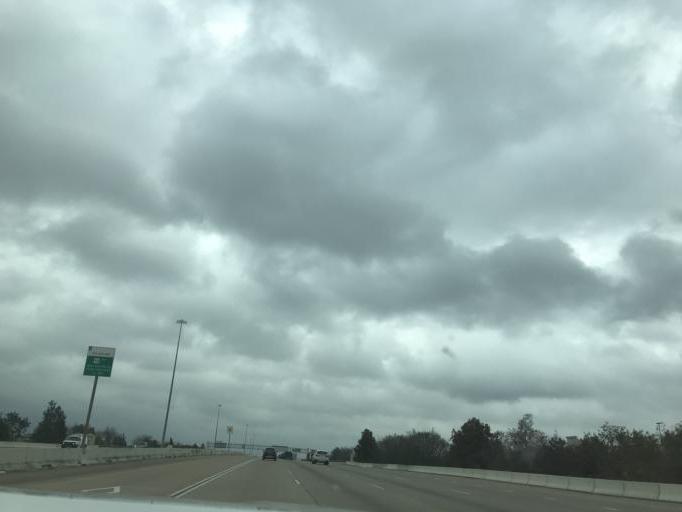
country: US
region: Texas
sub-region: Fort Bend County
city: Sugar Land
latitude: 29.5970
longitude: -95.6237
